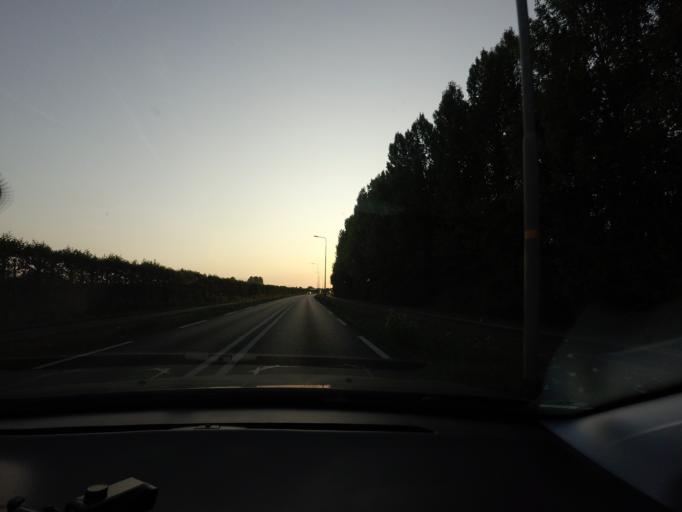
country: NL
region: Gelderland
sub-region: Gemeente Tiel
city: Tiel
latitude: 51.8868
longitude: 5.3952
